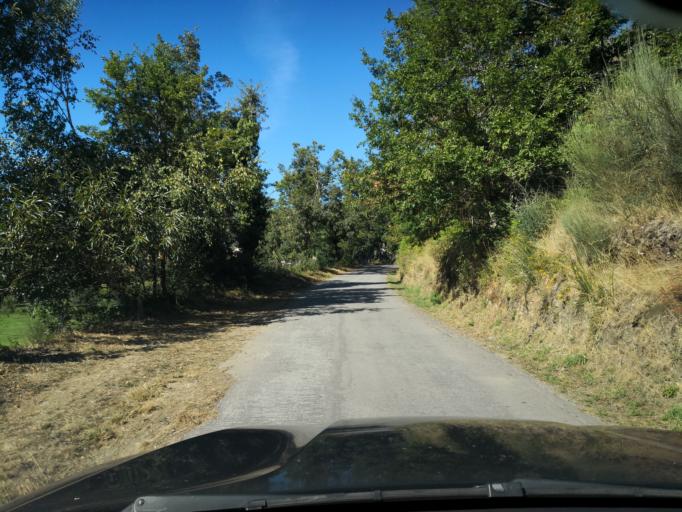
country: PT
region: Vila Real
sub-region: Santa Marta de Penaguiao
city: Santa Marta de Penaguiao
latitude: 41.2977
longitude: -7.8670
